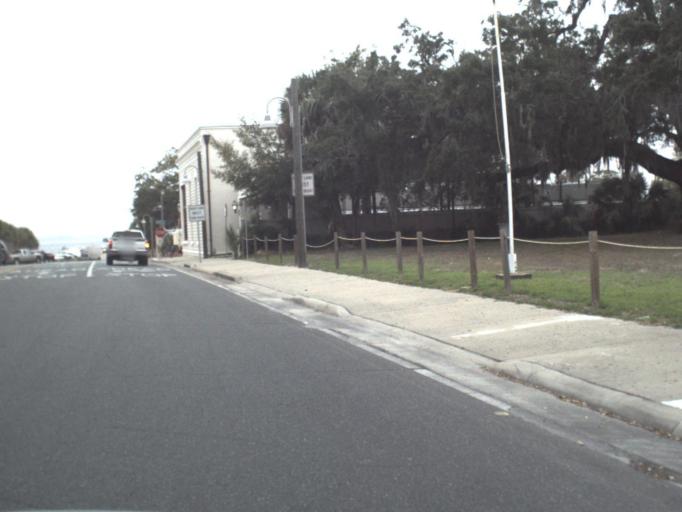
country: US
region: Florida
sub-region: Bay County
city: Pretty Bayou
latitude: 30.1675
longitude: -85.7006
